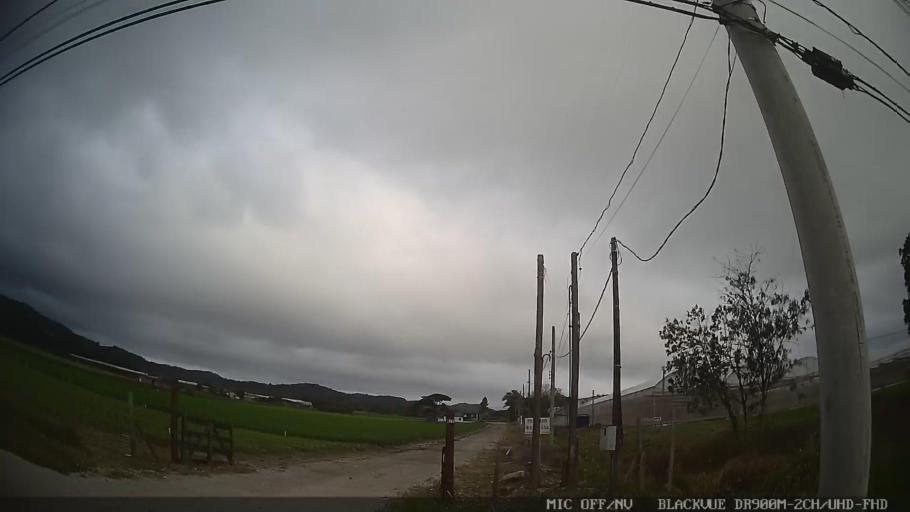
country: BR
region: Sao Paulo
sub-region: Biritiba-Mirim
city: Biritiba Mirim
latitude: -23.5548
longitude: -46.0860
